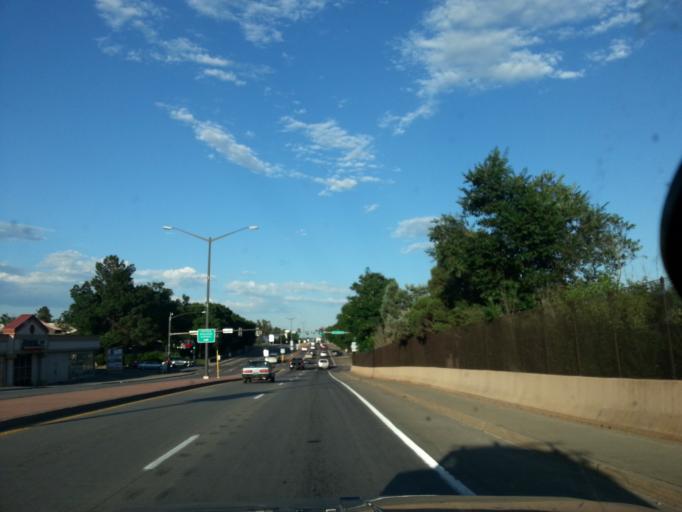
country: US
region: Colorado
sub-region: Larimer County
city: Loveland
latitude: 40.4072
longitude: -105.0757
